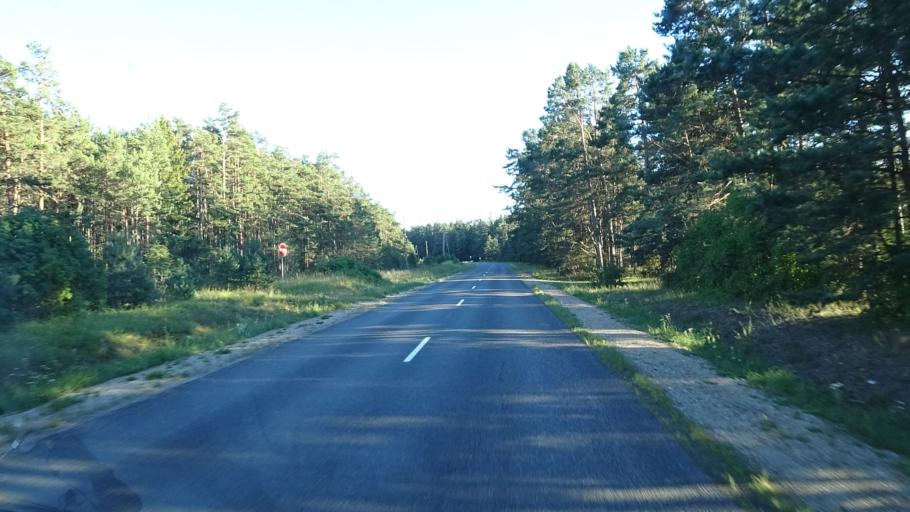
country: LV
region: Dundaga
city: Dundaga
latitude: 57.6806
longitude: 22.5692
